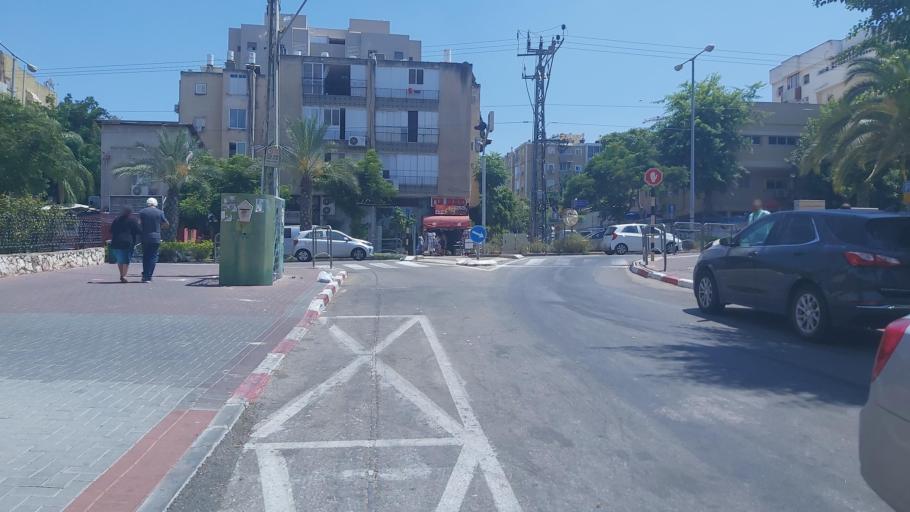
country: IL
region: Central District
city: Rishon LeZiyyon
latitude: 31.9624
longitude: 34.8094
